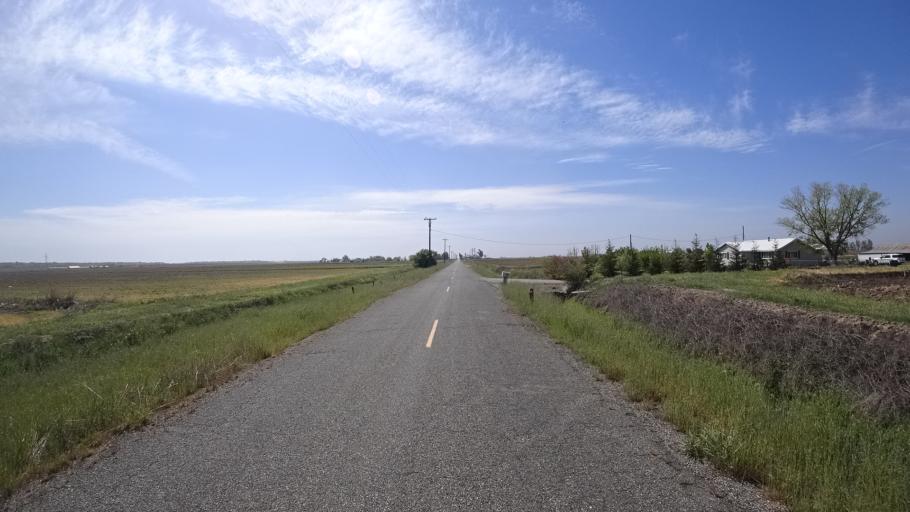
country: US
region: California
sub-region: Glenn County
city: Hamilton City
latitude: 39.5917
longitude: -122.0276
